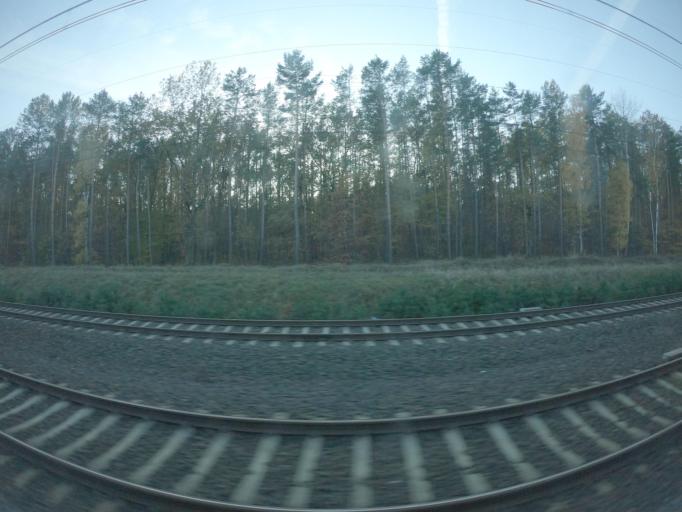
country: PL
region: Lubusz
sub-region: Powiat slubicki
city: Rzepin
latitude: 52.3139
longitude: 14.8586
